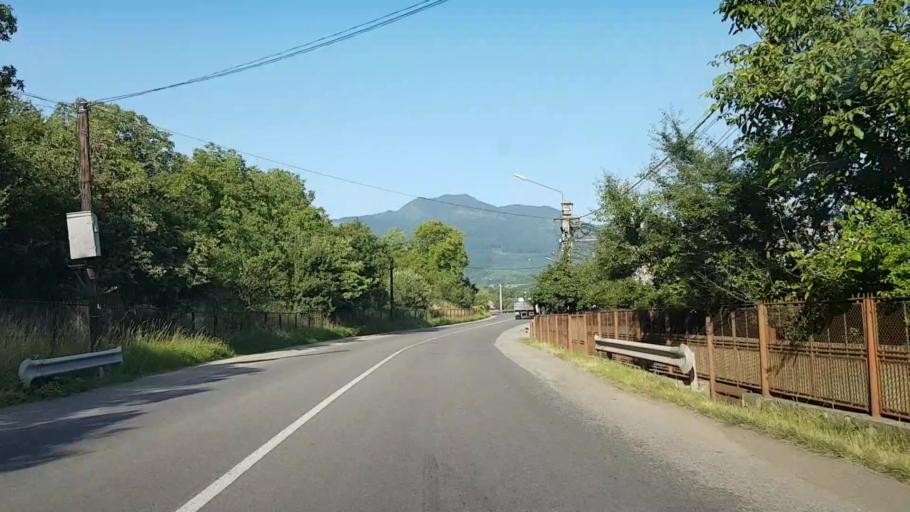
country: RO
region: Bistrita-Nasaud
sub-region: Comuna Tiha Bargaului
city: Tureac
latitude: 47.2300
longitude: 24.7865
